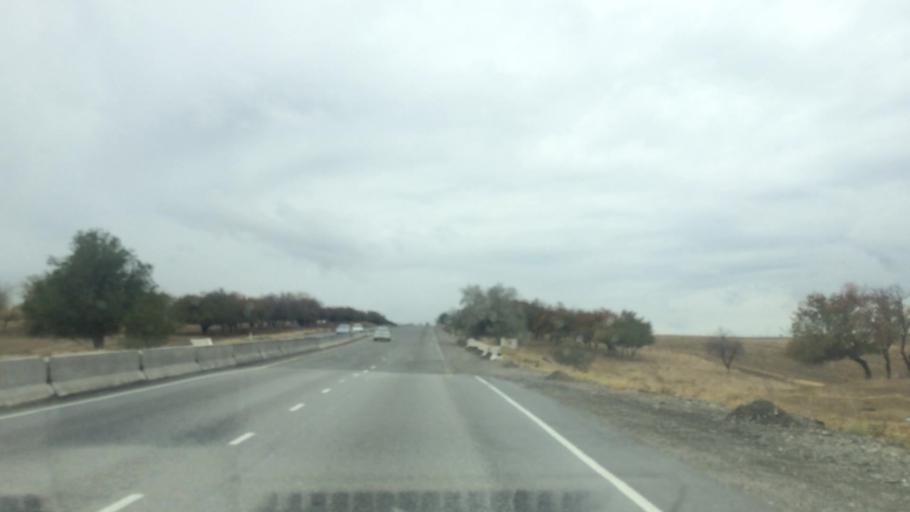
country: UZ
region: Samarqand
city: Bulung'ur
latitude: 39.8625
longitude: 67.4715
